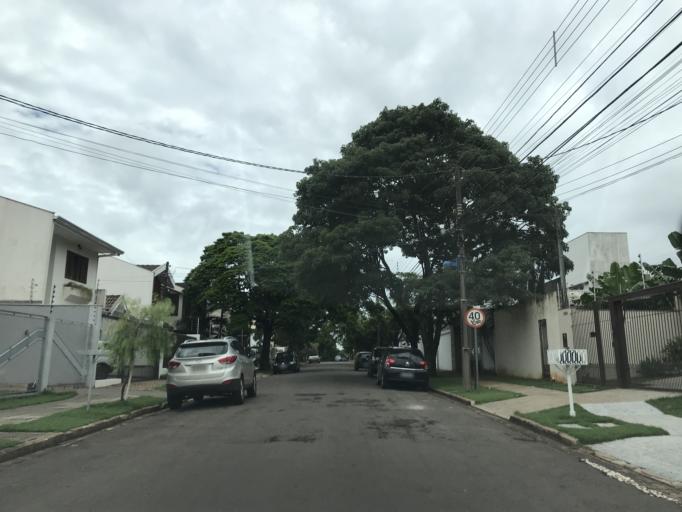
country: BR
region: Parana
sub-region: Maringa
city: Maringa
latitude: -23.4474
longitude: -51.9557
